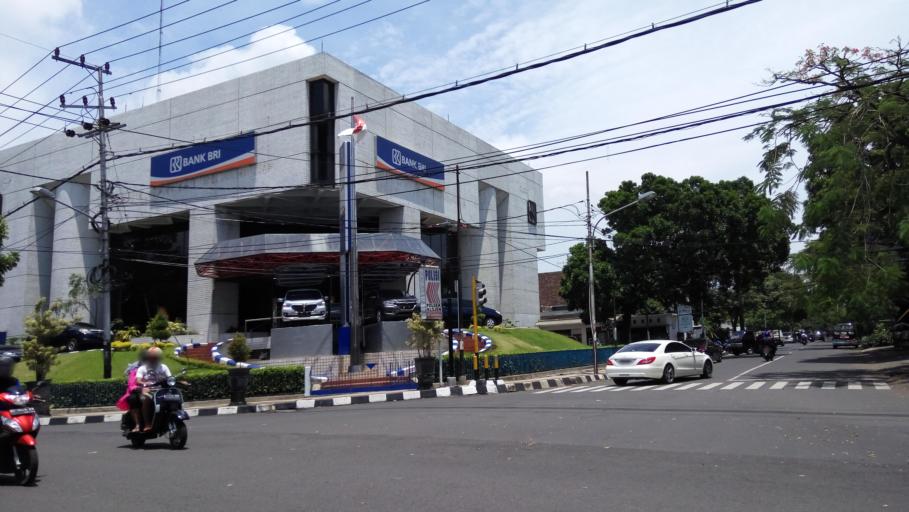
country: ID
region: East Java
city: Malang
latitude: -7.9802
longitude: 112.6263
